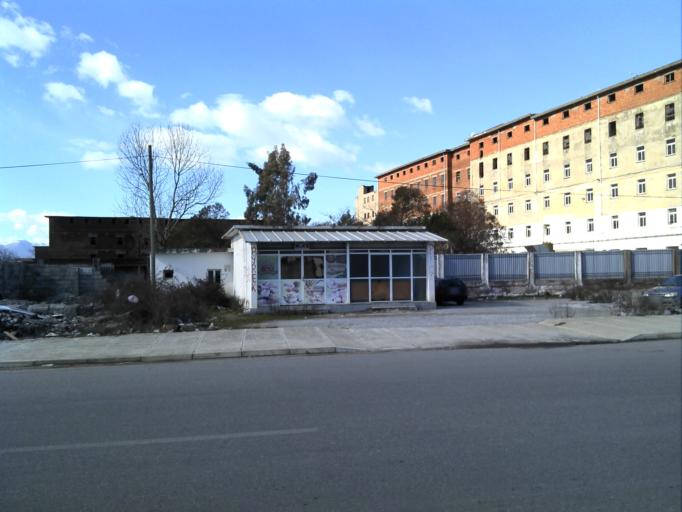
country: AL
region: Shkoder
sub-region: Rrethi i Shkodres
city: Shkoder
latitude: 42.0854
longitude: 19.5306
